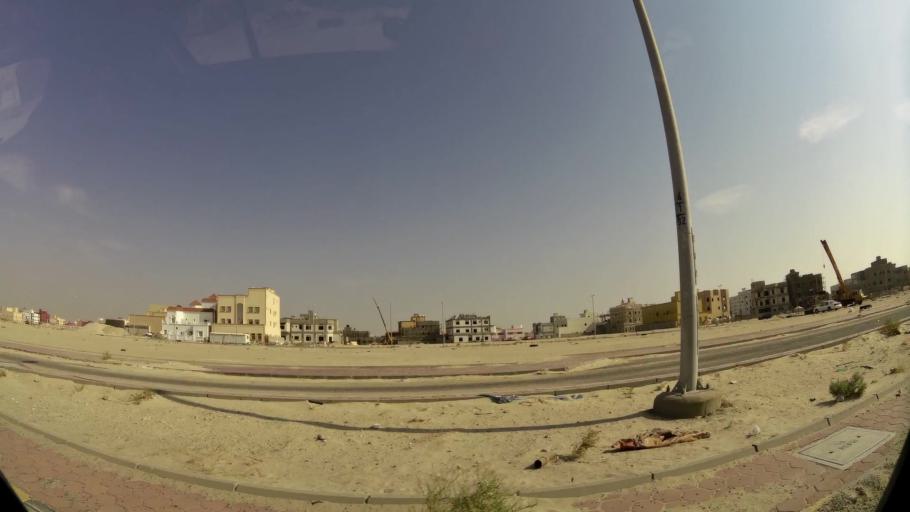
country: KW
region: Al Ahmadi
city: Al Wafrah
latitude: 28.7865
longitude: 48.0477
